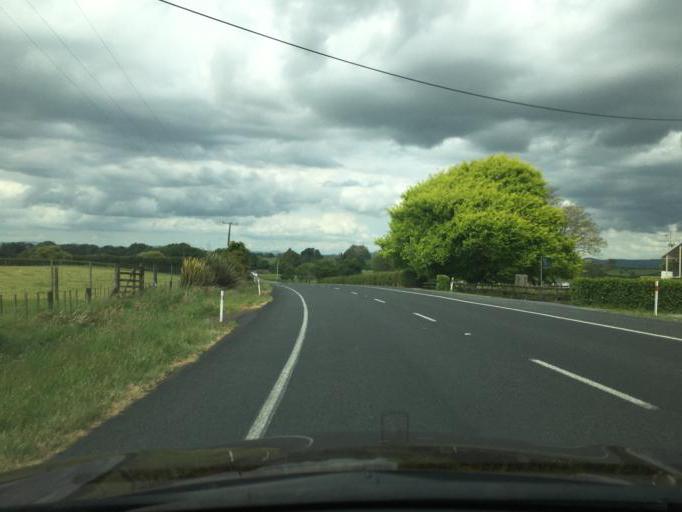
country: NZ
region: Waikato
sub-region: Waipa District
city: Cambridge
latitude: -38.0064
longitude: 175.3769
